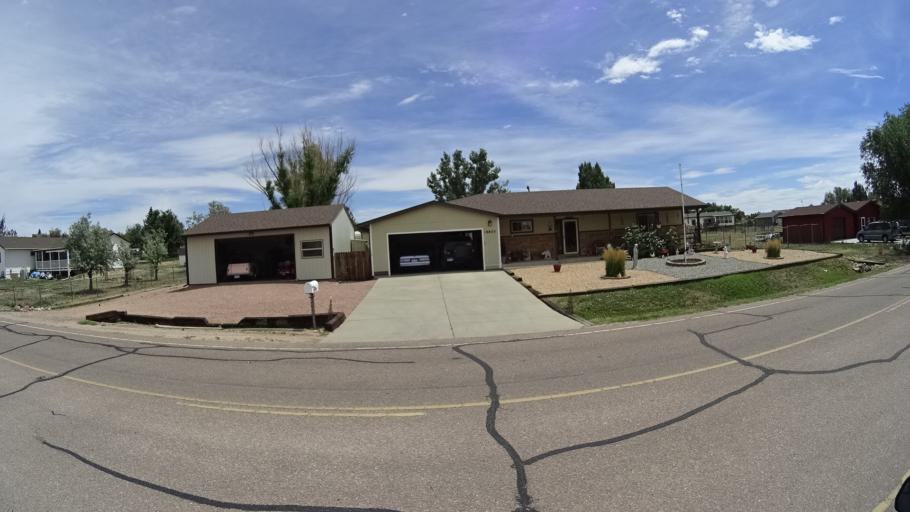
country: US
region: Colorado
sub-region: El Paso County
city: Fountain
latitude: 38.6747
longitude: -104.6736
